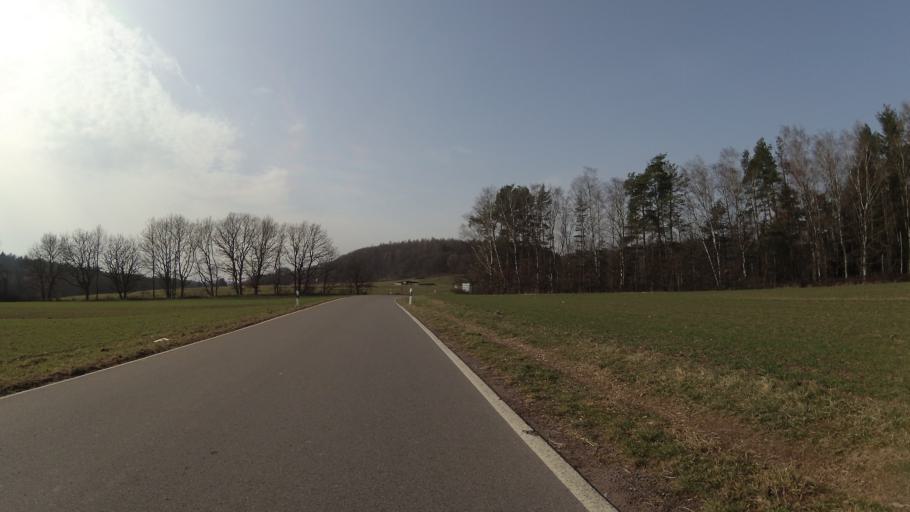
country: DE
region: Saarland
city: Beckingen
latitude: 49.4086
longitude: 6.7297
